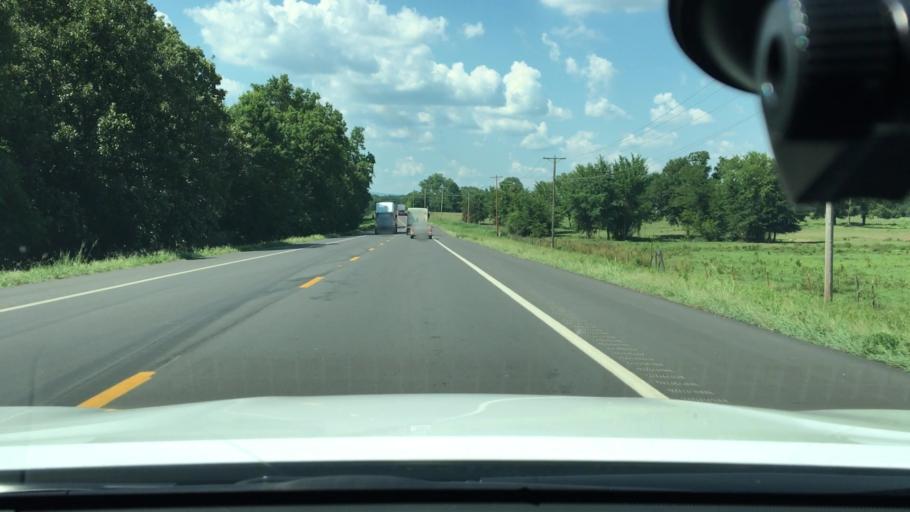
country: US
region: Arkansas
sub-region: Johnson County
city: Clarksville
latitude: 35.4434
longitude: -93.5291
